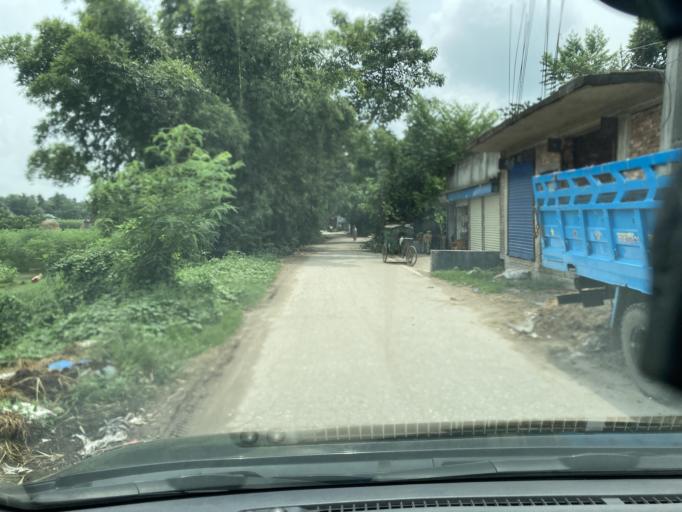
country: BD
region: Dhaka
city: Dohar
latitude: 23.7612
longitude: 90.1981
